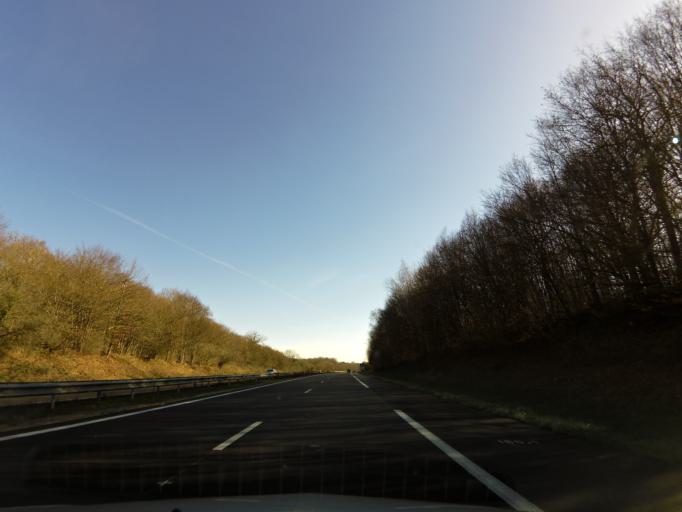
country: FR
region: Bourgogne
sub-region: Departement de l'Yonne
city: Joux-la-Ville
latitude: 47.6868
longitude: 3.8486
